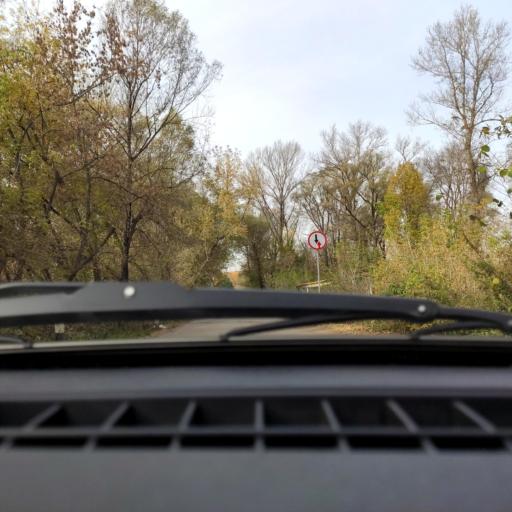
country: RU
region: Bashkortostan
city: Ufa
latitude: 54.7850
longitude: 56.1646
